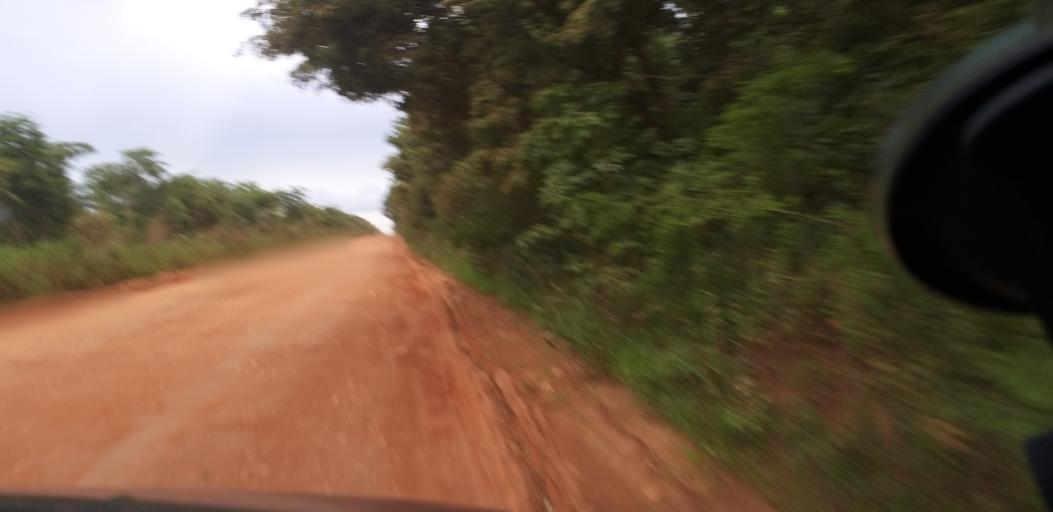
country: ZM
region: Lusaka
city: Lusaka
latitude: -15.2047
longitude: 28.4375
